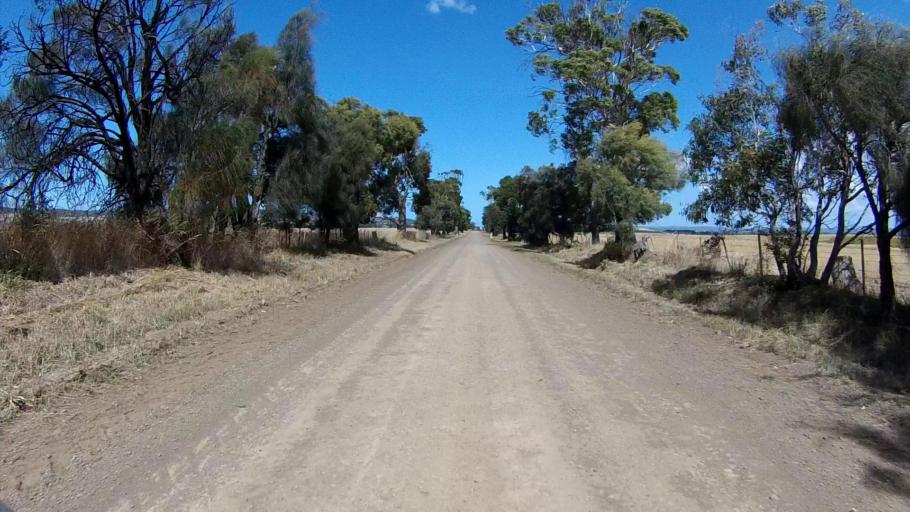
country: AU
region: Tasmania
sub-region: Break O'Day
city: St Helens
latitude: -41.9897
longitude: 148.0667
